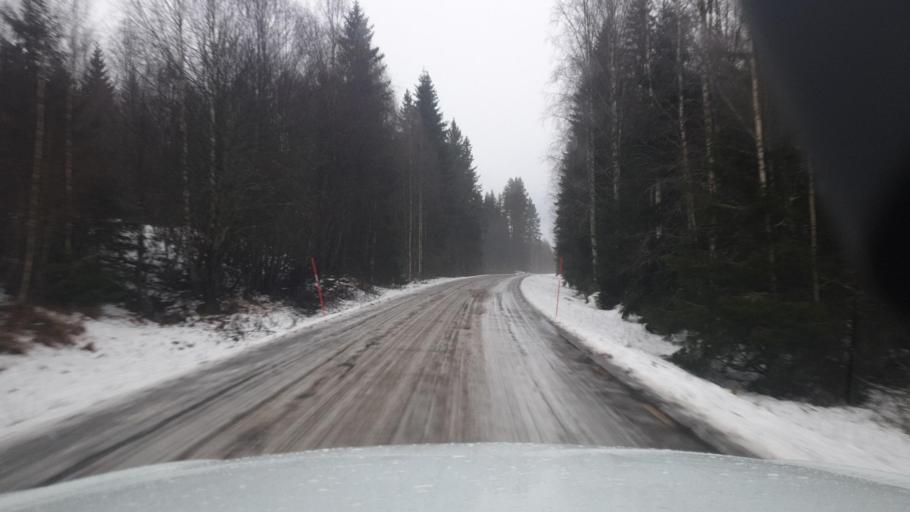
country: SE
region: Vaermland
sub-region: Torsby Kommun
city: Torsby
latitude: 60.0074
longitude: 12.6945
